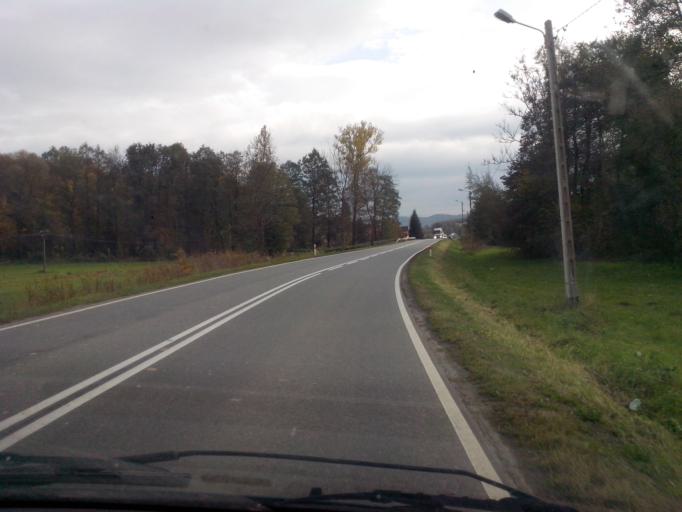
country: PL
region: Subcarpathian Voivodeship
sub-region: Powiat strzyzowski
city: Wisniowa
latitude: 49.8964
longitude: 21.6430
